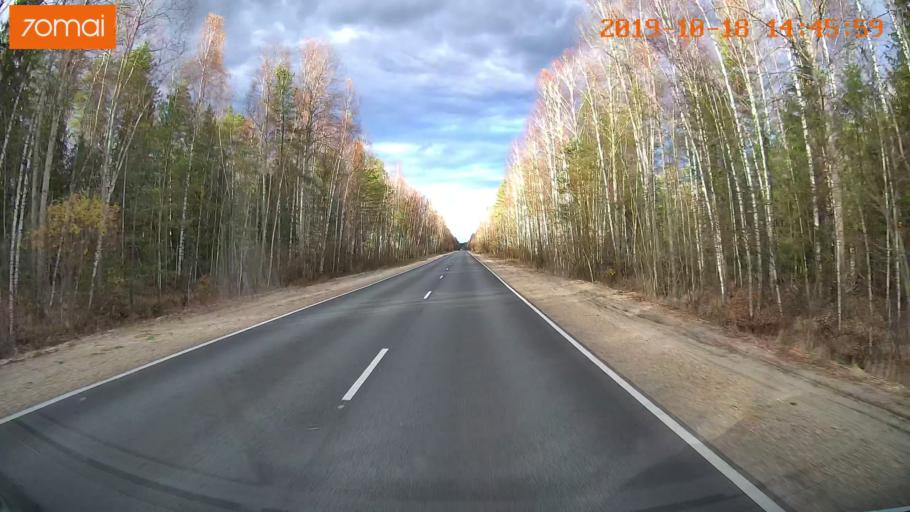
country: RU
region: Vladimir
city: Velikodvorskiy
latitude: 55.3639
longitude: 40.6800
